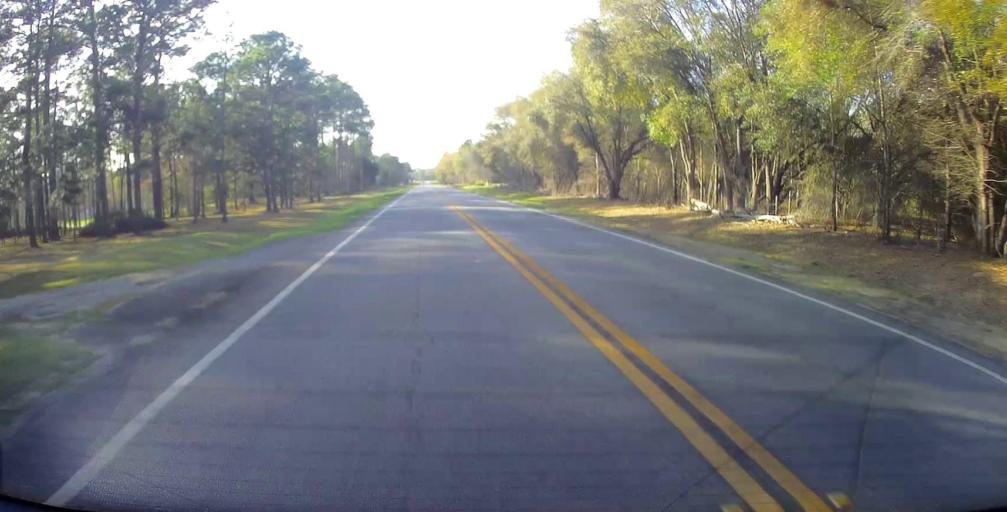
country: US
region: Georgia
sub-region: Toombs County
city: Lyons
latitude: 32.1803
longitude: -82.2911
